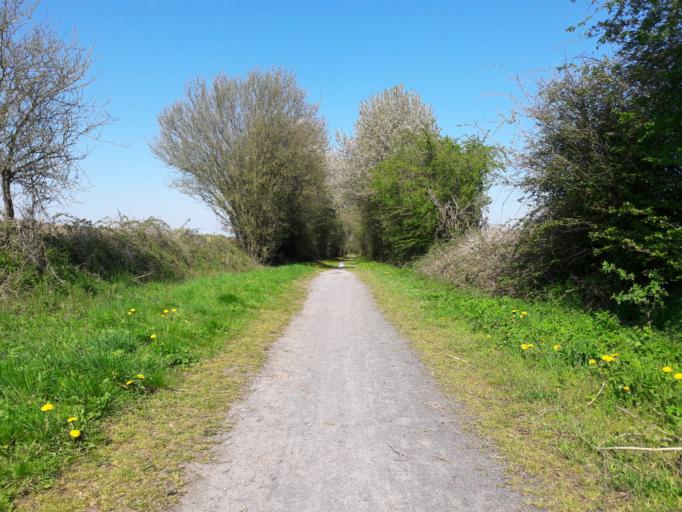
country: FR
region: Nord-Pas-de-Calais
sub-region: Departement du Nord
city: Sains-du-Nord
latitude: 50.1658
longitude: 4.0736
